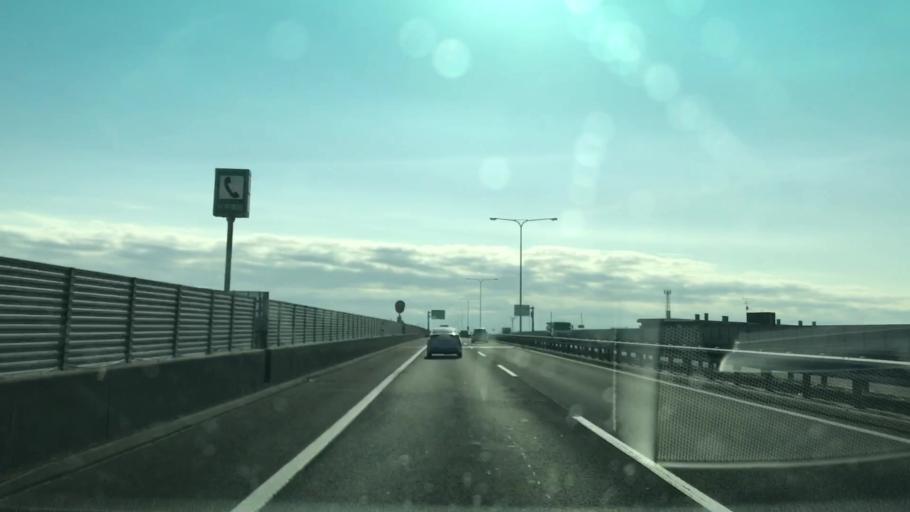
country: JP
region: Hokkaido
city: Sapporo
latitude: 43.0522
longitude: 141.4303
